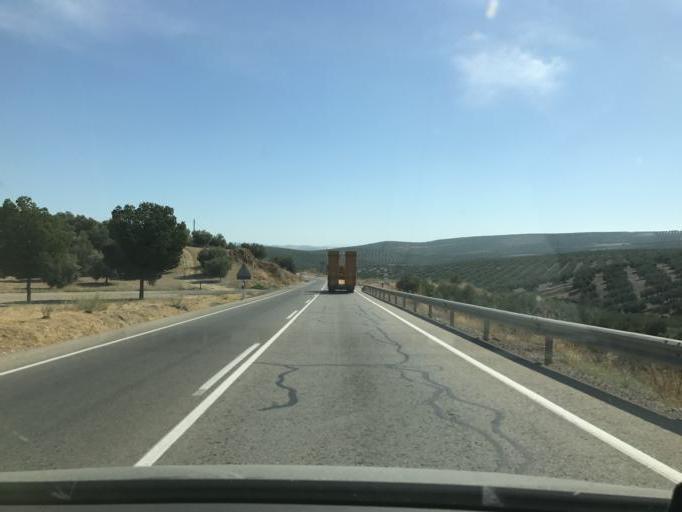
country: ES
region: Andalusia
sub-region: Province of Cordoba
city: Espejo
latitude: 37.6822
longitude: -4.5174
